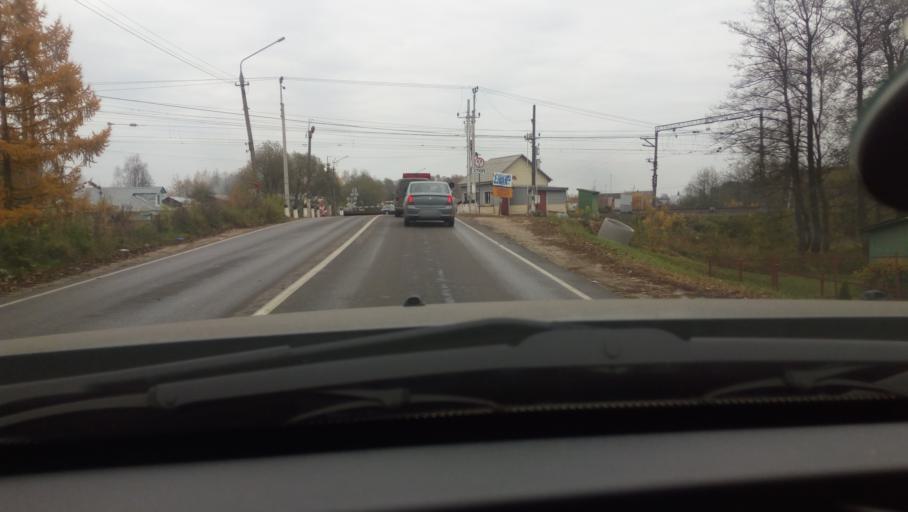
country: RU
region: Moskovskaya
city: Likino-Dulevo
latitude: 55.7004
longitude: 38.9444
